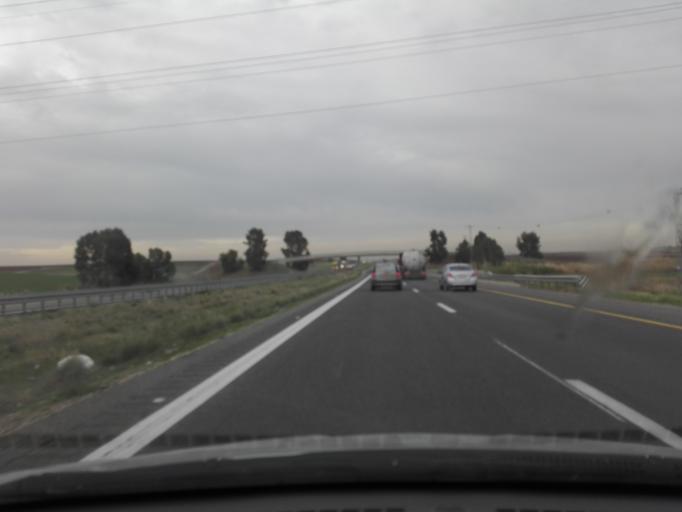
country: IL
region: Central District
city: Mazkeret Batya
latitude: 31.8358
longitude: 34.8583
